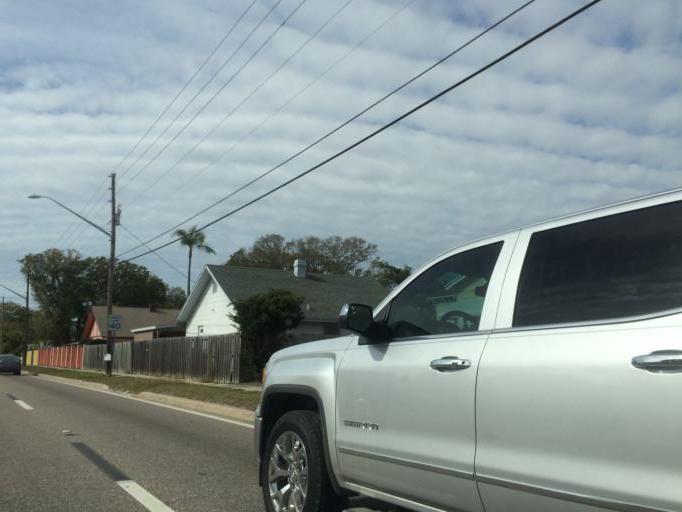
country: US
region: Florida
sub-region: Pinellas County
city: West and East Lealman
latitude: 27.8065
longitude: -82.6862
